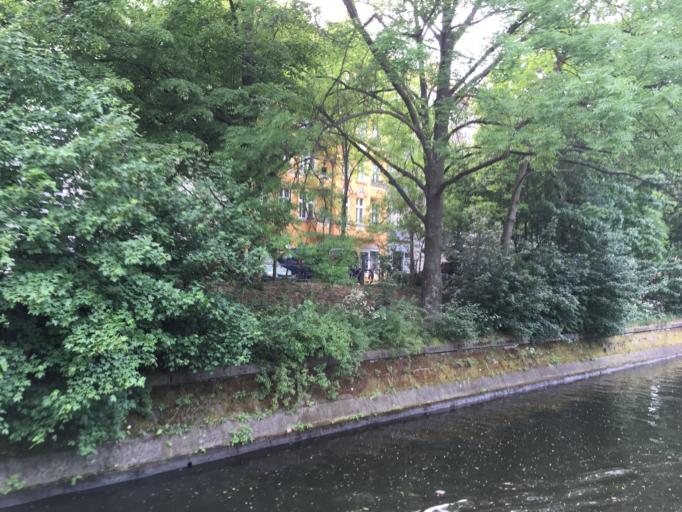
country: DE
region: Berlin
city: Berlin Treptow
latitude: 52.4942
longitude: 13.4268
